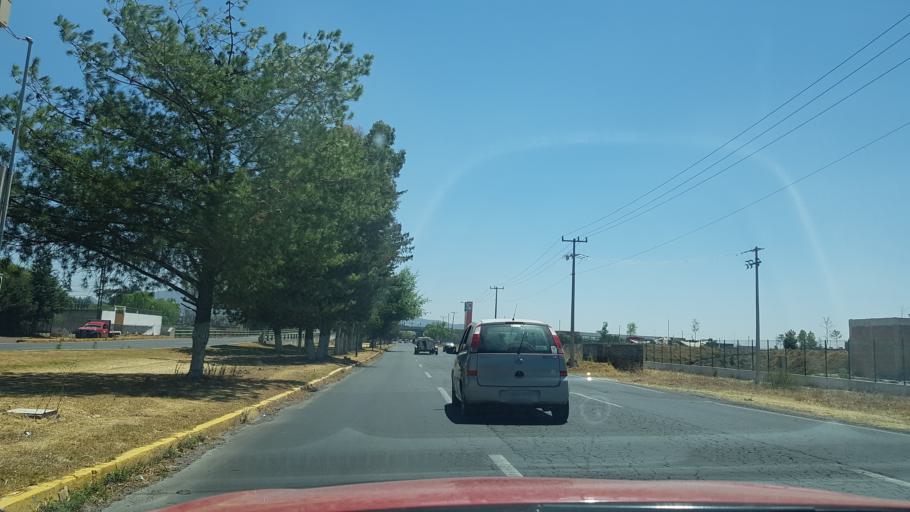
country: MX
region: Mexico
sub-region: Atlacomulco
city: Santa Cruz Bombatevi
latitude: 19.7951
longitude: -99.8908
